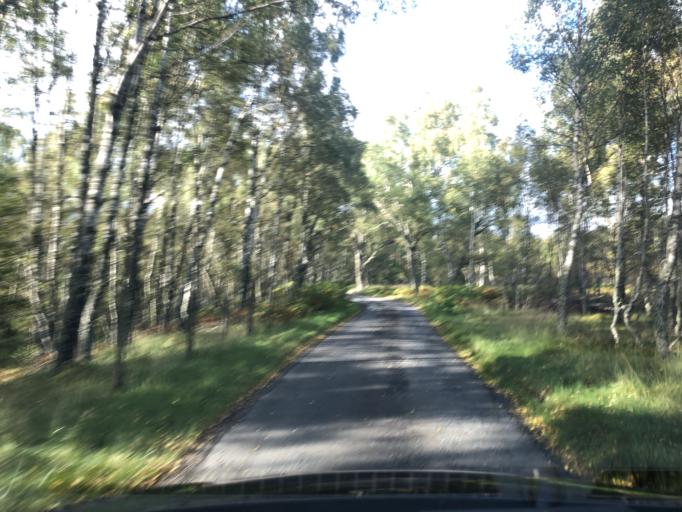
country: GB
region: Scotland
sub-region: Highland
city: Aviemore
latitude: 57.0637
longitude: -3.8982
